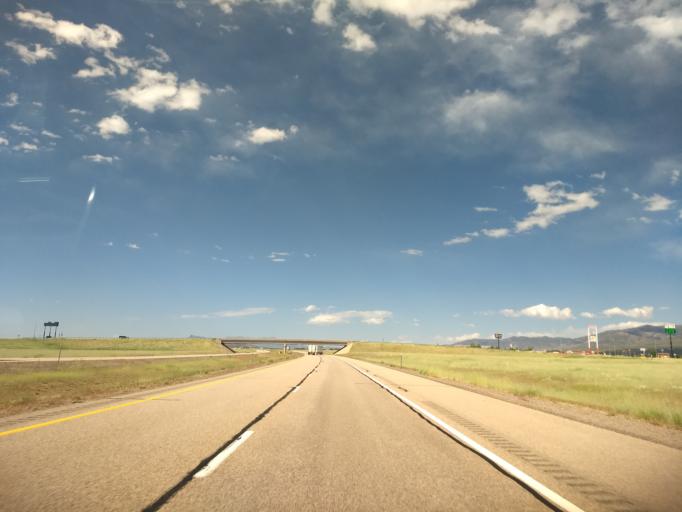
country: US
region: Utah
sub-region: Millard County
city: Fillmore
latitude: 38.9459
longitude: -112.3510
